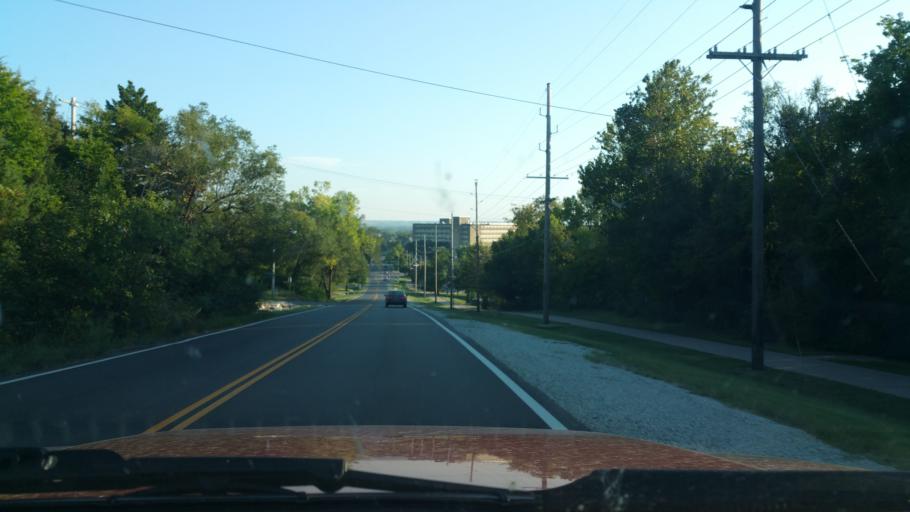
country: US
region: Kansas
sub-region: Riley County
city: Manhattan
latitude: 39.1991
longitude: -96.5764
